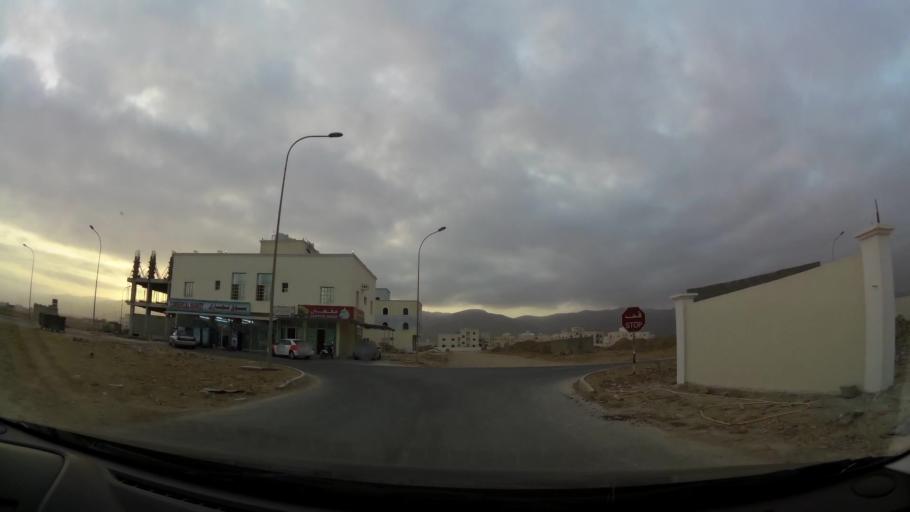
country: OM
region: Zufar
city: Salalah
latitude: 17.0317
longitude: 54.0184
